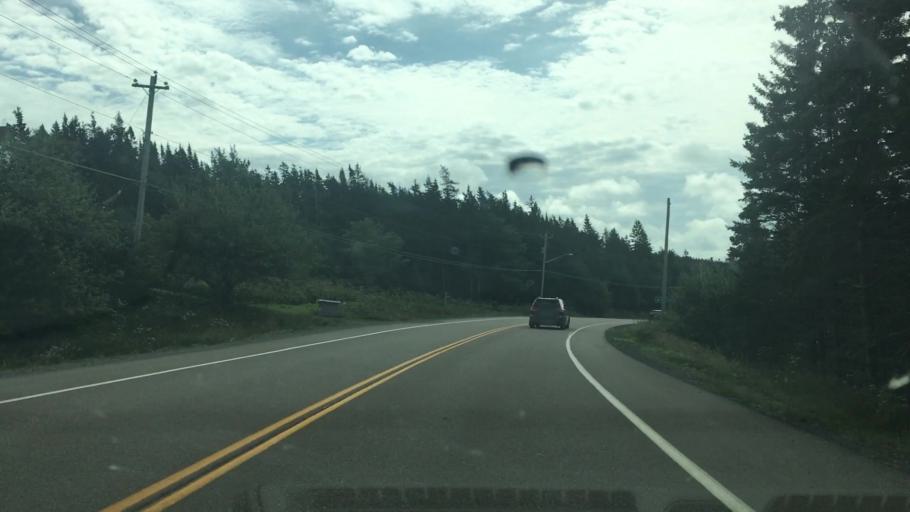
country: CA
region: Nova Scotia
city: Princeville
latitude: 45.7022
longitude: -60.7383
